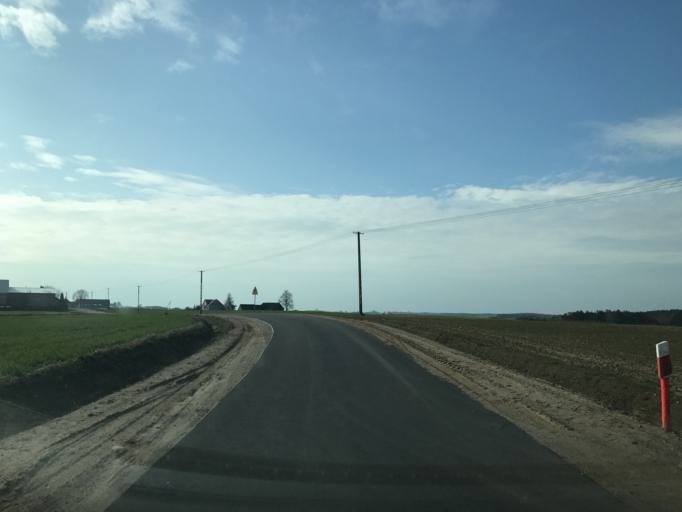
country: PL
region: Warmian-Masurian Voivodeship
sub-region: Powiat dzialdowski
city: Lidzbark
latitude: 53.3181
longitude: 19.8470
